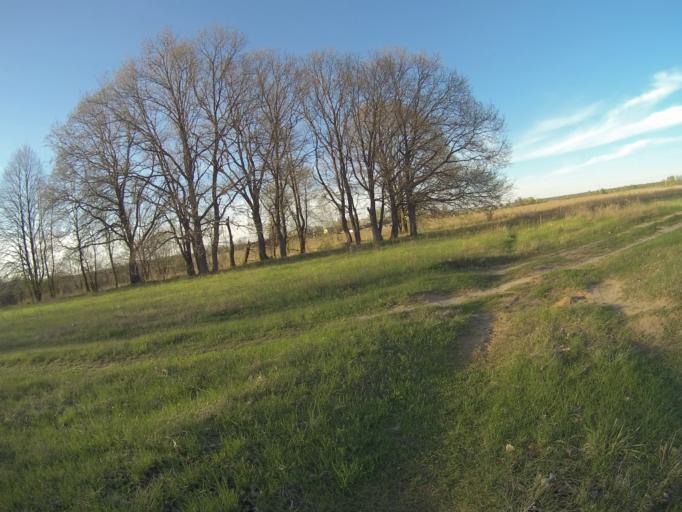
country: RU
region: Vladimir
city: Raduzhnyy
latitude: 56.0305
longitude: 40.2924
